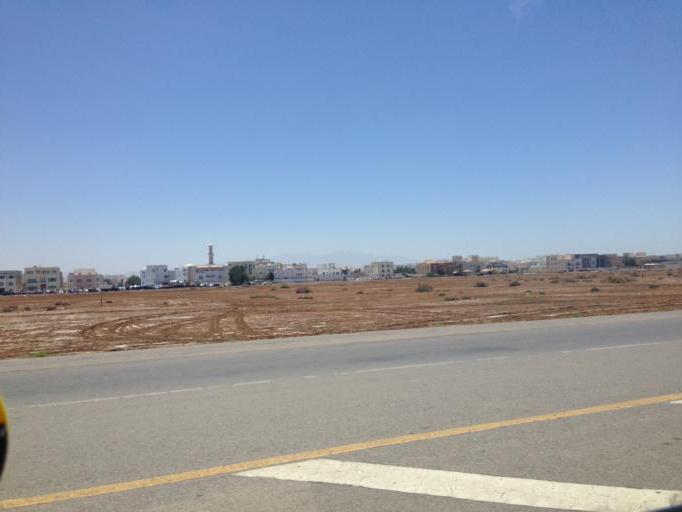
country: OM
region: Muhafazat Masqat
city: As Sib al Jadidah
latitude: 23.6275
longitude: 58.2597
